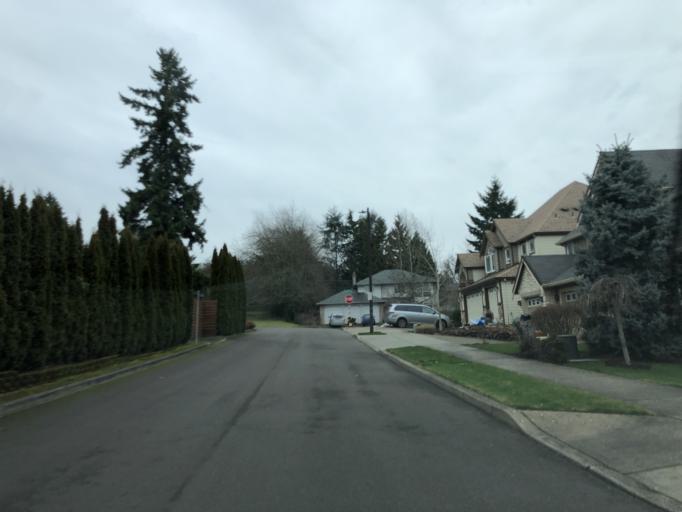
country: US
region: Oregon
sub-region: Washington County
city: Tigard
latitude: 45.4170
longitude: -122.7754
